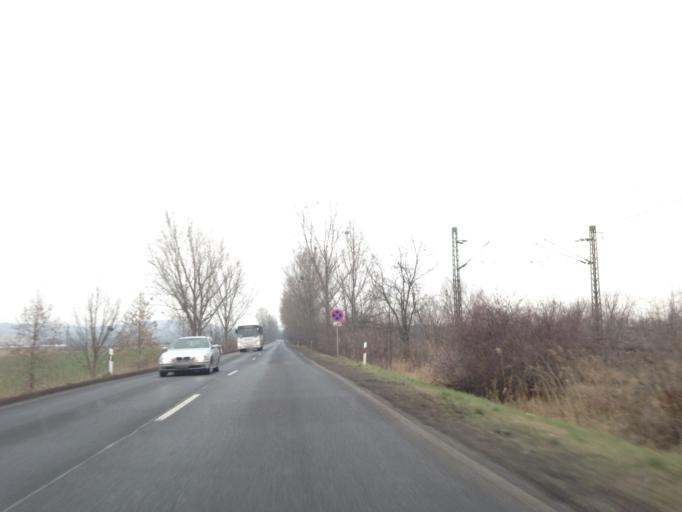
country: HU
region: Komarom-Esztergom
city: Almasfuzito
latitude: 47.7171
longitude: 18.2782
